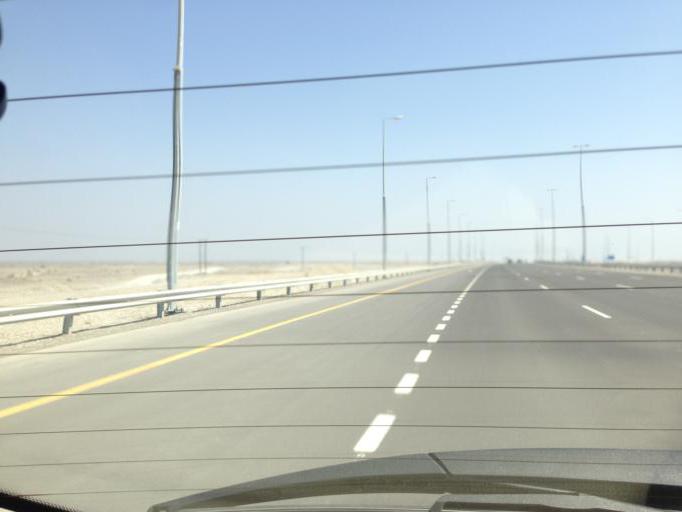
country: OM
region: Al Batinah
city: Barka'
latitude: 23.5536
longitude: 57.6889
